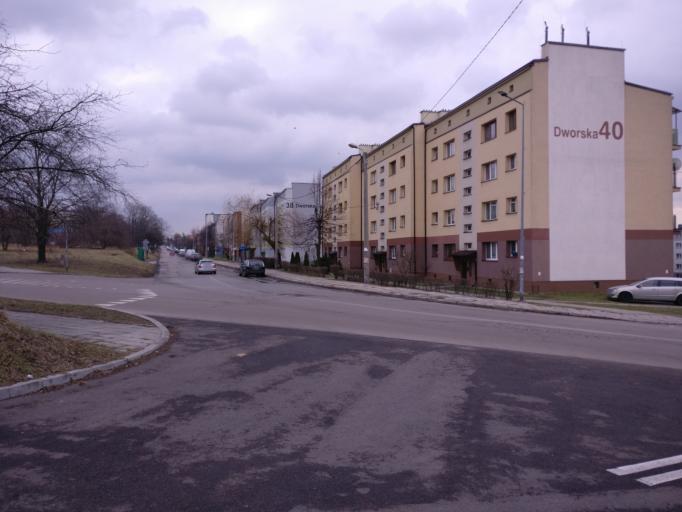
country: PL
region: Silesian Voivodeship
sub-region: Powiat bedzinski
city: Bedzin
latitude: 50.2985
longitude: 19.1763
